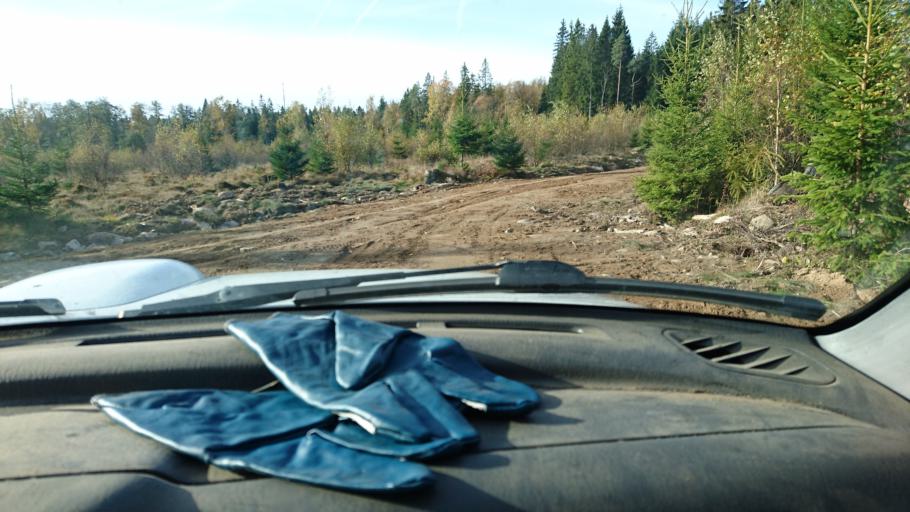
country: SE
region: Vaestra Goetaland
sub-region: Ulricehamns Kommun
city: Ulricehamn
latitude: 57.9366
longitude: 13.5599
